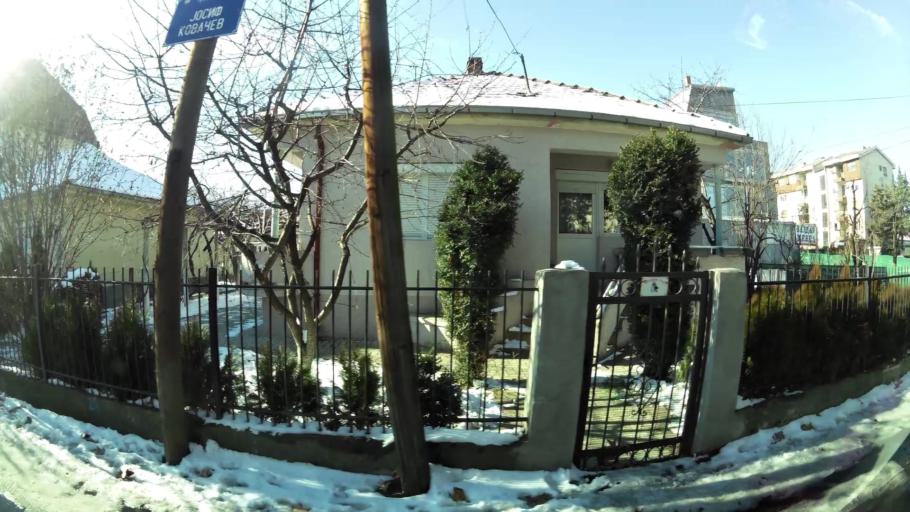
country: MK
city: Krushopek
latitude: 42.0062
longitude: 21.3566
